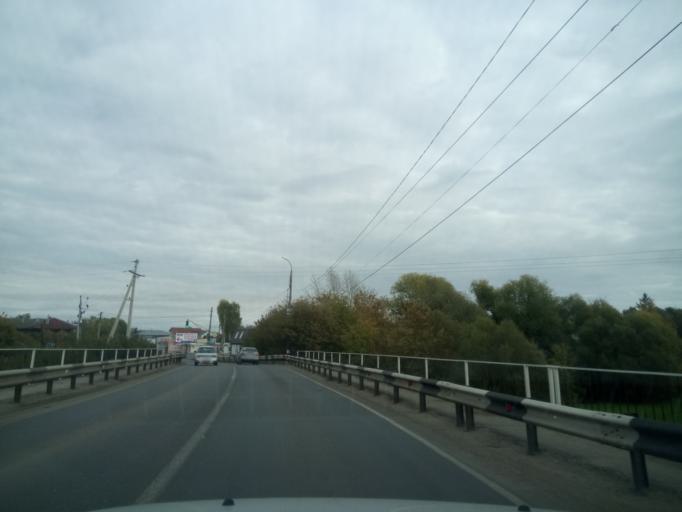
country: RU
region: Nizjnij Novgorod
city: Lukoyanov
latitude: 55.0297
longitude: 44.4899
